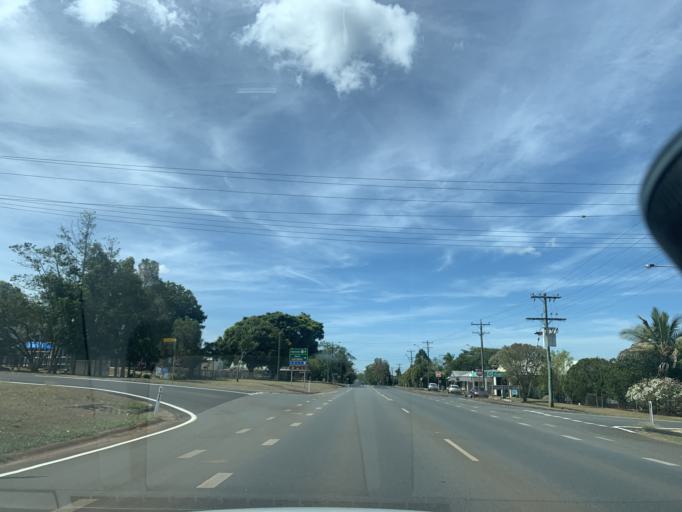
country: AU
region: Queensland
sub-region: Tablelands
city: Tolga
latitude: -17.2246
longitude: 145.4787
